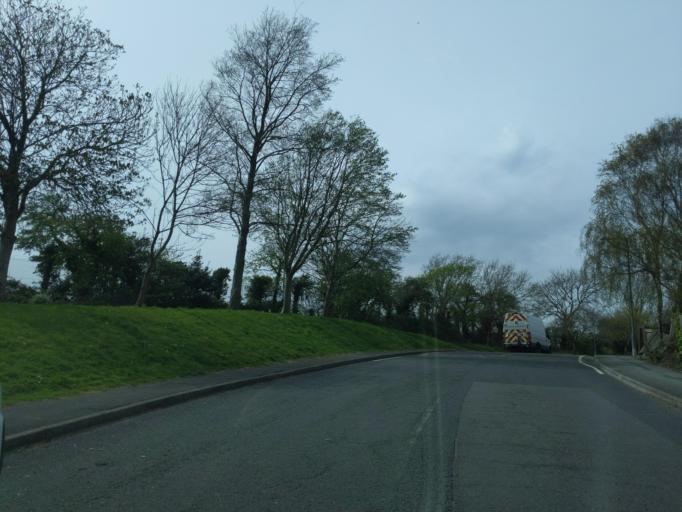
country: GB
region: England
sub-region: Cornwall
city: Torpoint
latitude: 50.3766
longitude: -4.2202
